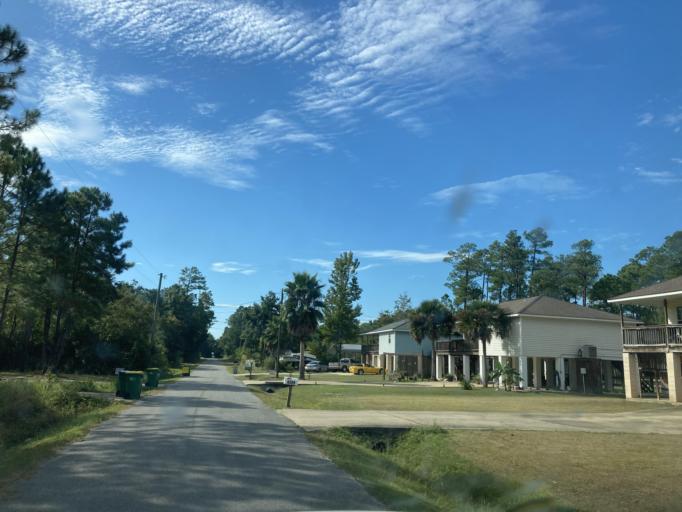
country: US
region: Mississippi
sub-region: Jackson County
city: Saint Martin
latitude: 30.4337
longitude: -88.8612
